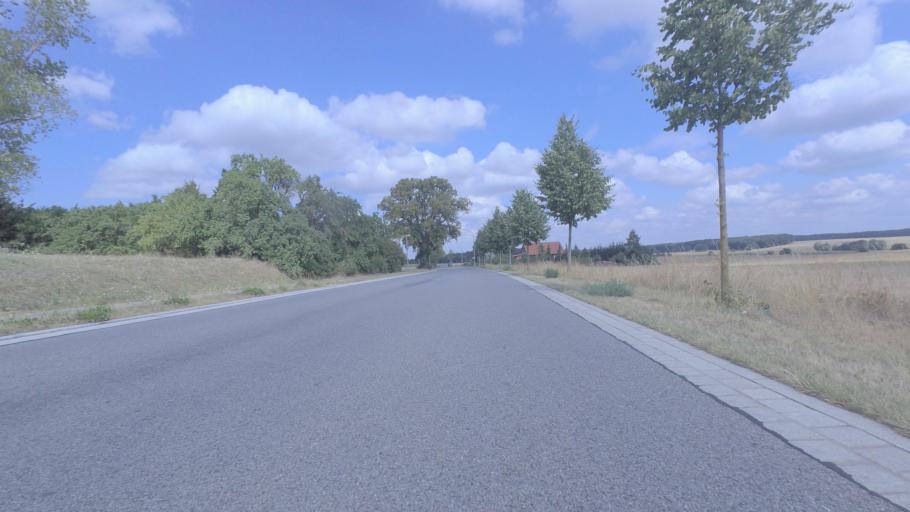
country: DE
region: Brandenburg
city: Walsleben
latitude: 52.9912
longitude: 12.6541
